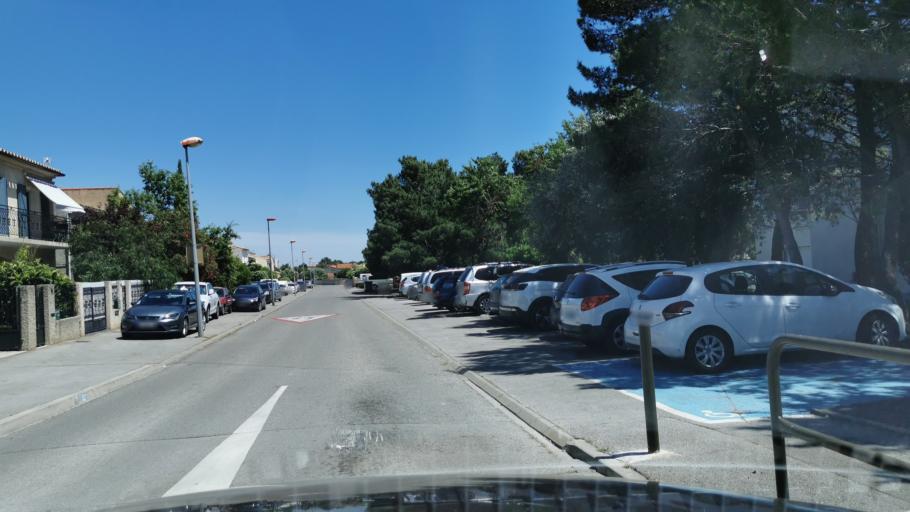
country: FR
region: Languedoc-Roussillon
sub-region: Departement de l'Aude
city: Narbonne
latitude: 43.1831
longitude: 2.9733
